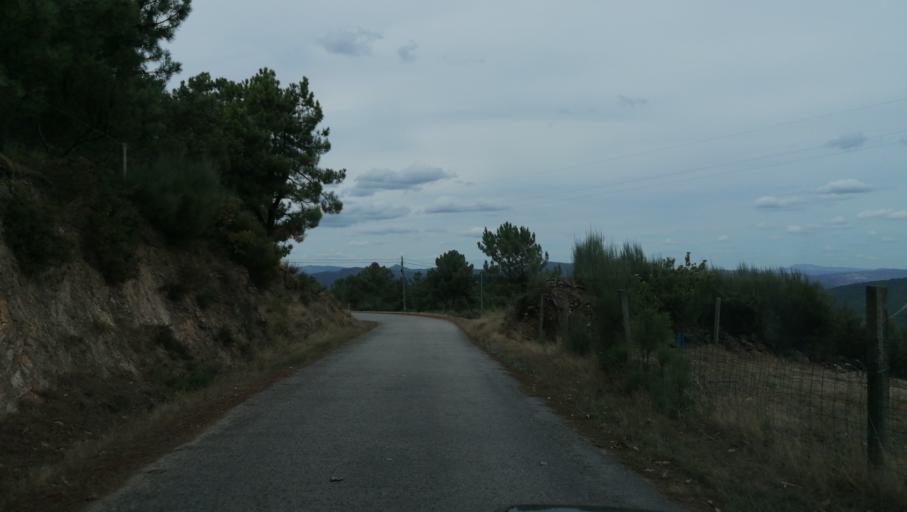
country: PT
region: Vila Real
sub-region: Vila Pouca de Aguiar
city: Vila Pouca de Aguiar
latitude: 41.5616
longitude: -7.6614
